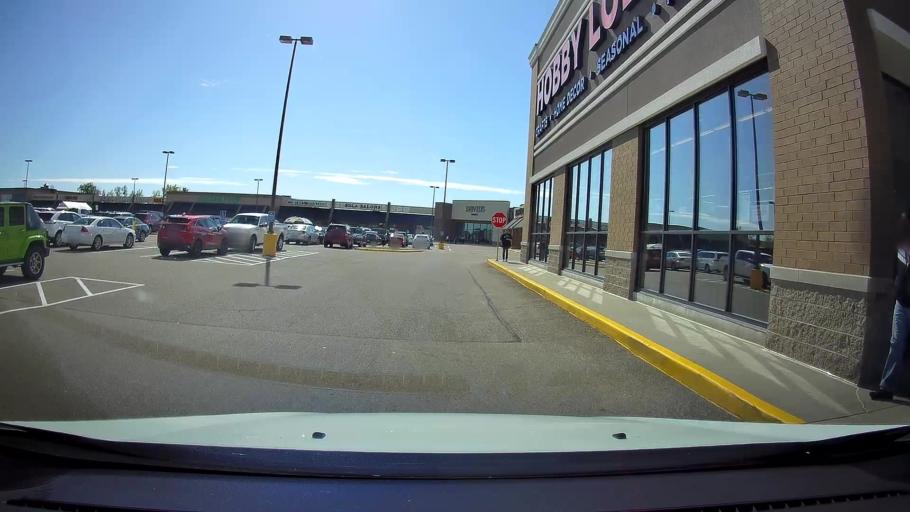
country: US
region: Minnesota
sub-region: Ramsey County
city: Roseville
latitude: 45.0140
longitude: -93.1798
